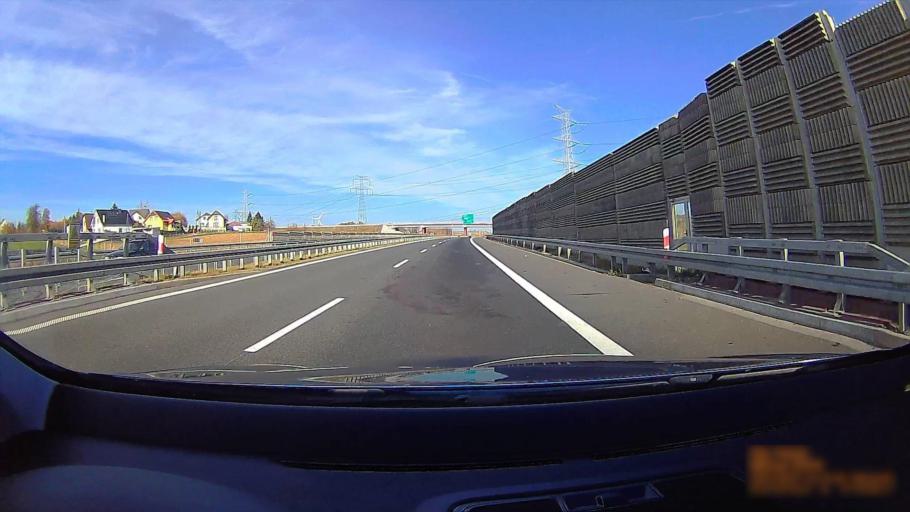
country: PL
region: Greater Poland Voivodeship
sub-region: Powiat ostrowski
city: Przygodzice
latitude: 51.6207
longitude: 17.8621
